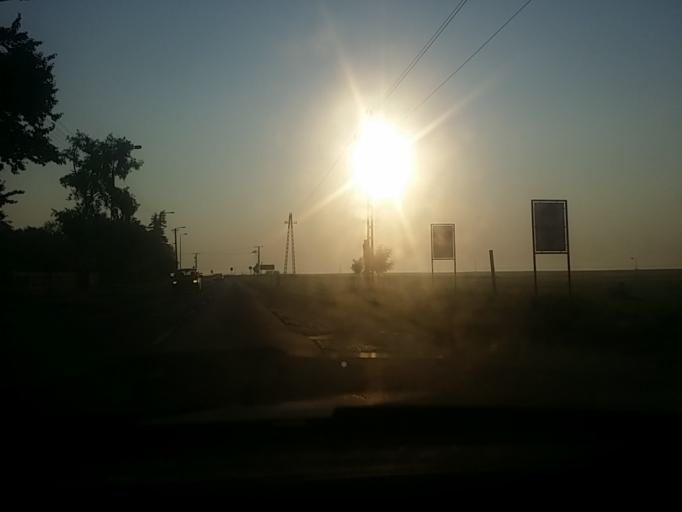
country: HU
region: Pest
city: Nagykata
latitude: 47.4163
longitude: 19.7532
